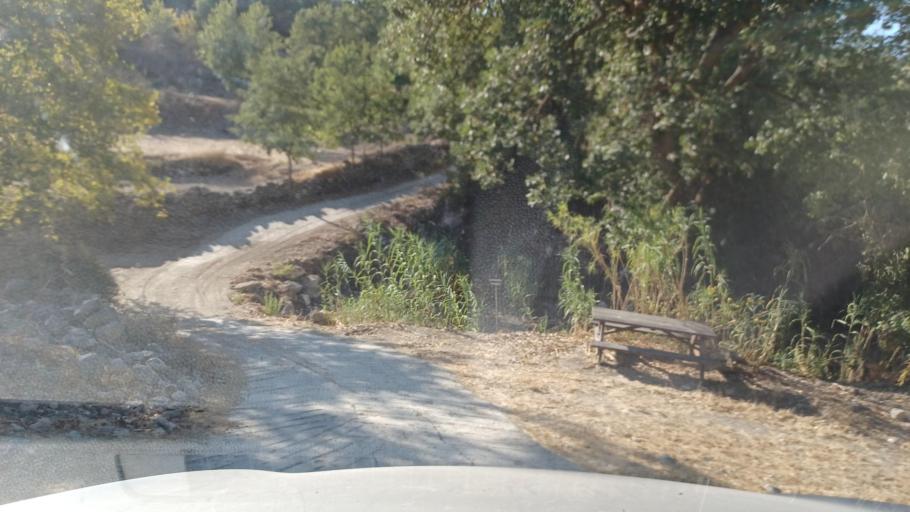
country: CY
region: Pafos
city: Polis
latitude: 34.9976
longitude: 32.4877
